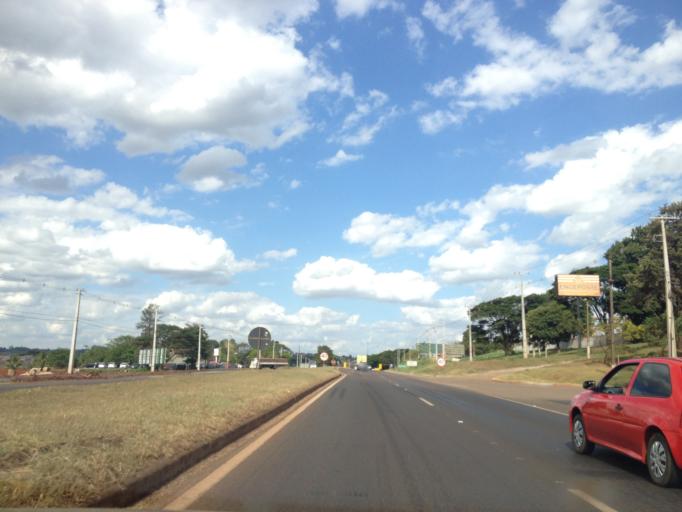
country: BR
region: Parana
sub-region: Marialva
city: Marialva
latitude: -23.4641
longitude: -51.8322
